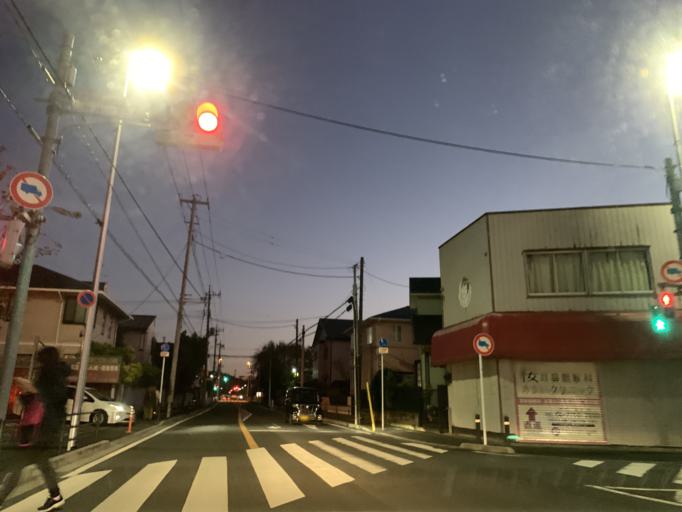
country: JP
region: Chiba
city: Nagareyama
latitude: 35.8952
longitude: 139.9090
